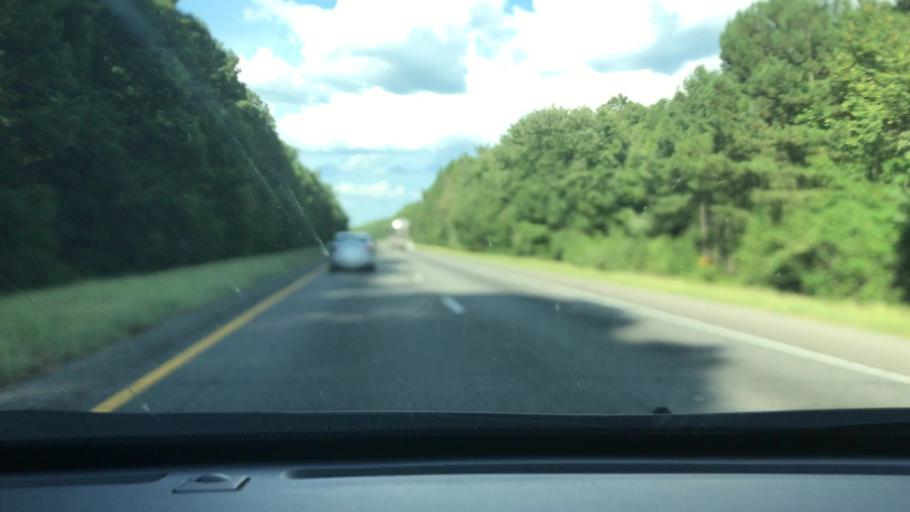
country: US
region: South Carolina
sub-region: Dillon County
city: Latta
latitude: 34.3180
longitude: -79.5924
